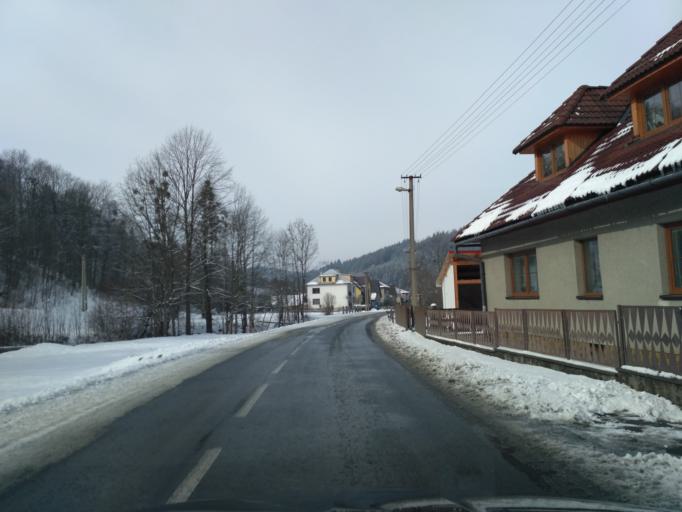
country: CZ
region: Zlin
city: Valasska Bystrice
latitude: 49.4172
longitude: 18.1045
